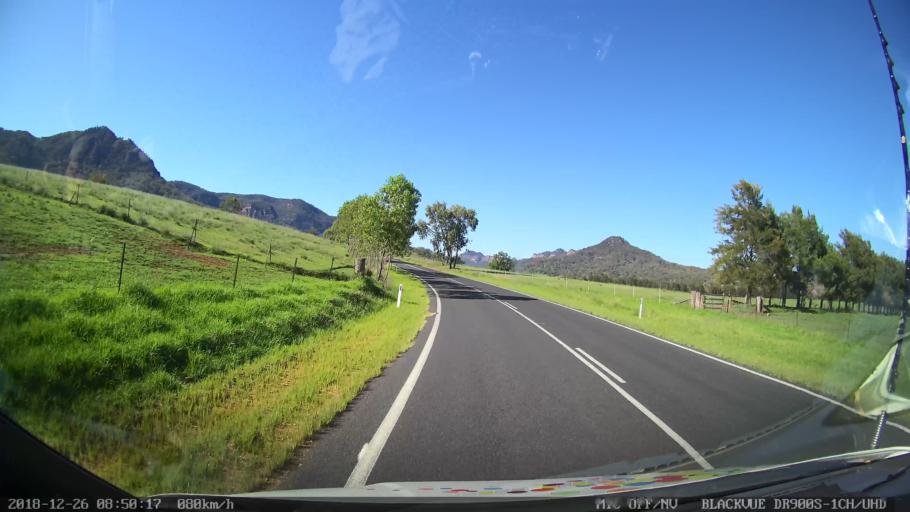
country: AU
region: New South Wales
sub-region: Mid-Western Regional
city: Kandos
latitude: -32.5740
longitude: 150.0956
